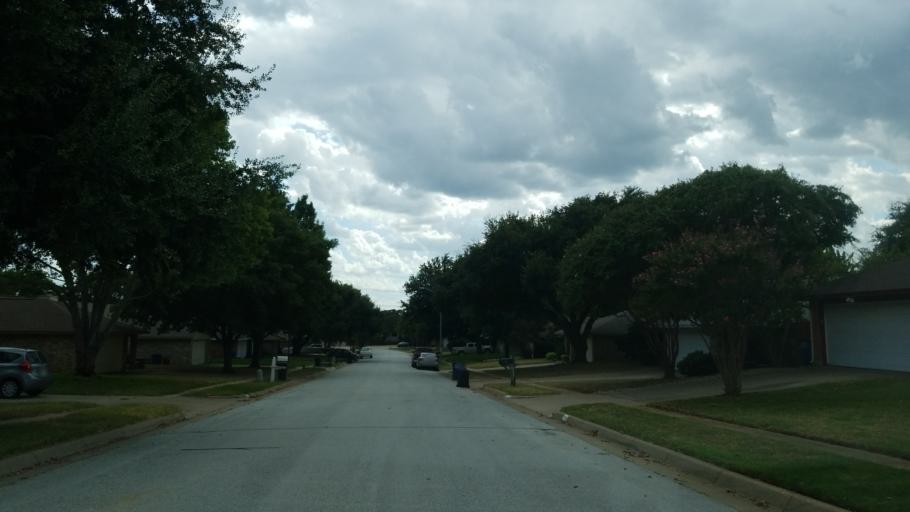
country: US
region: Texas
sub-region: Tarrant County
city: Euless
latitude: 32.8720
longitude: -97.0765
